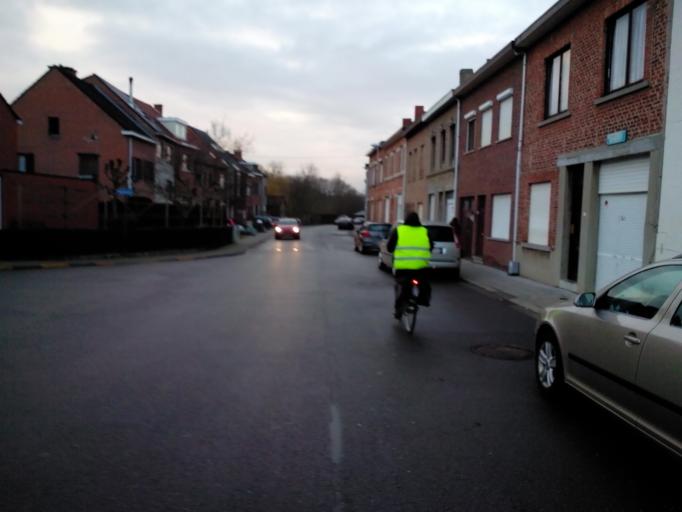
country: BE
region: Flanders
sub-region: Provincie Vlaams-Brabant
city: Leuven
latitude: 50.8650
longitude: 4.7092
